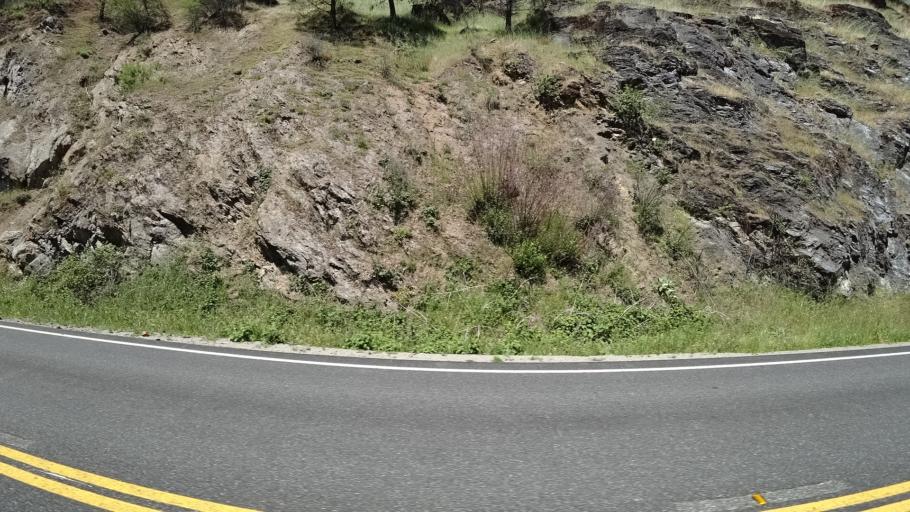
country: US
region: California
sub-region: Trinity County
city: Weaverville
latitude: 40.7663
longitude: -123.1053
